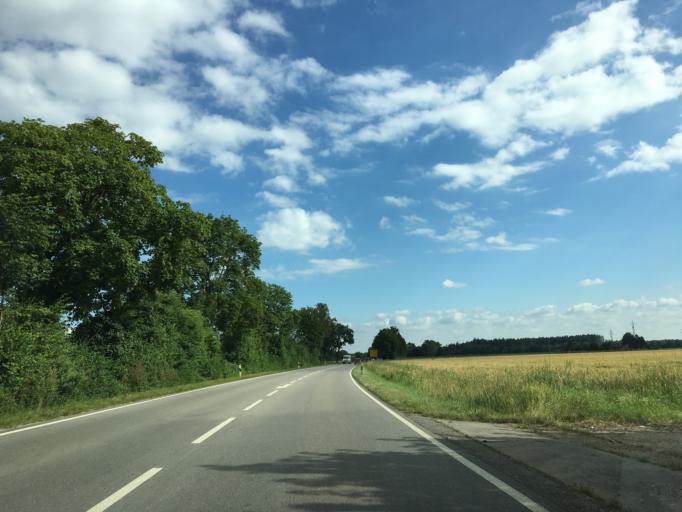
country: DE
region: Bavaria
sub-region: Upper Bavaria
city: Sauerlach
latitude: 47.9511
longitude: 11.6505
